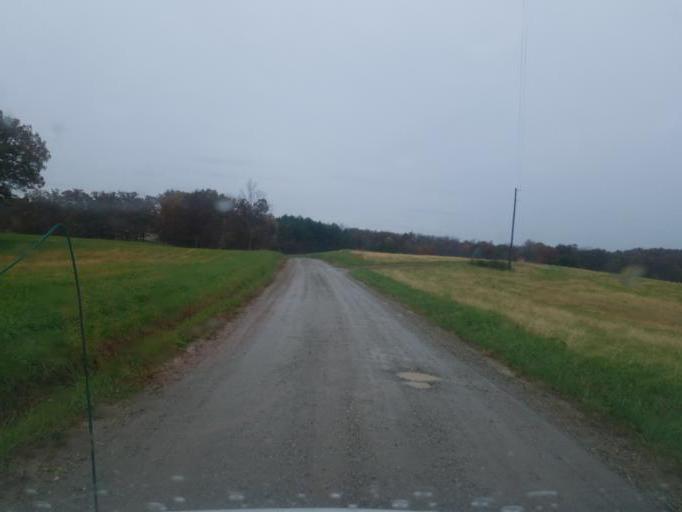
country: US
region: Ohio
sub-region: Washington County
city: Beverly
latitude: 39.4686
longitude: -81.6578
